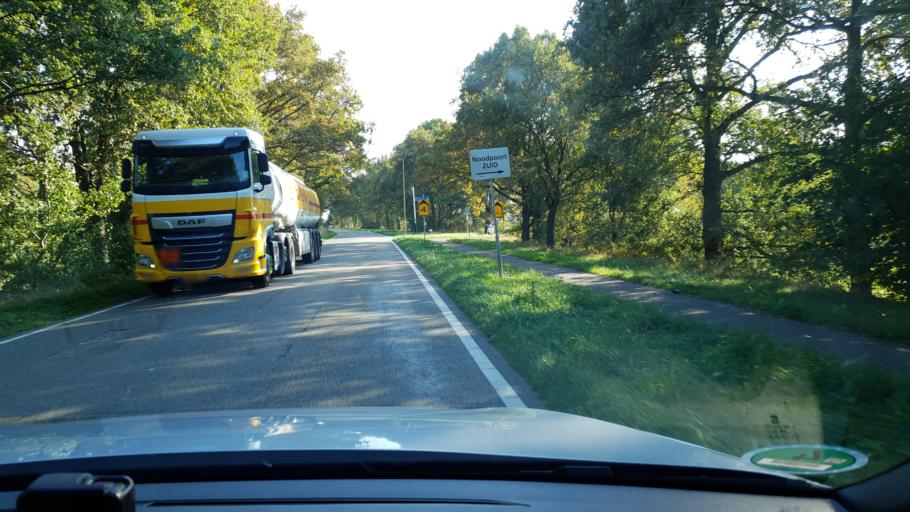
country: NL
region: North Brabant
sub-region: Gemeente Eindhoven
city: Meerhoven
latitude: 51.4690
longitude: 5.3917
